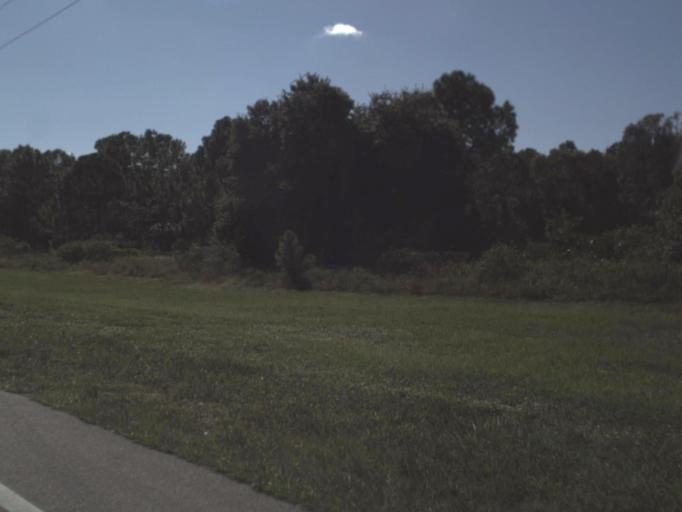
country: US
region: Florida
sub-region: Lee County
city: Gateway
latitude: 26.5802
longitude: -81.7101
